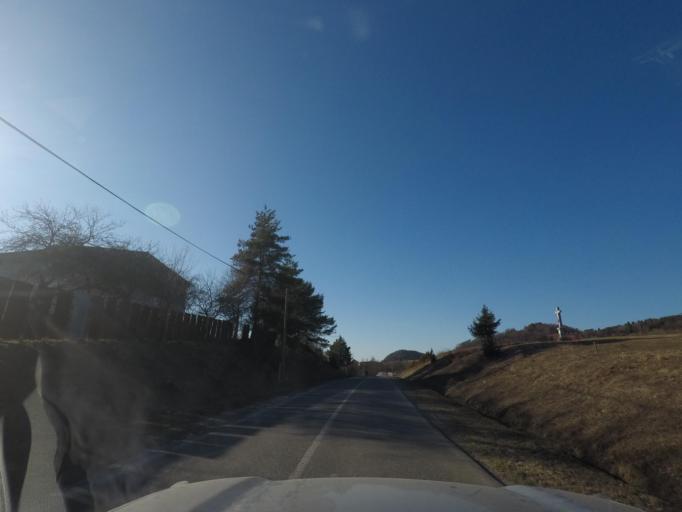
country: SK
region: Presovsky
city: Medzilaborce
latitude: 49.2207
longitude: 21.9775
